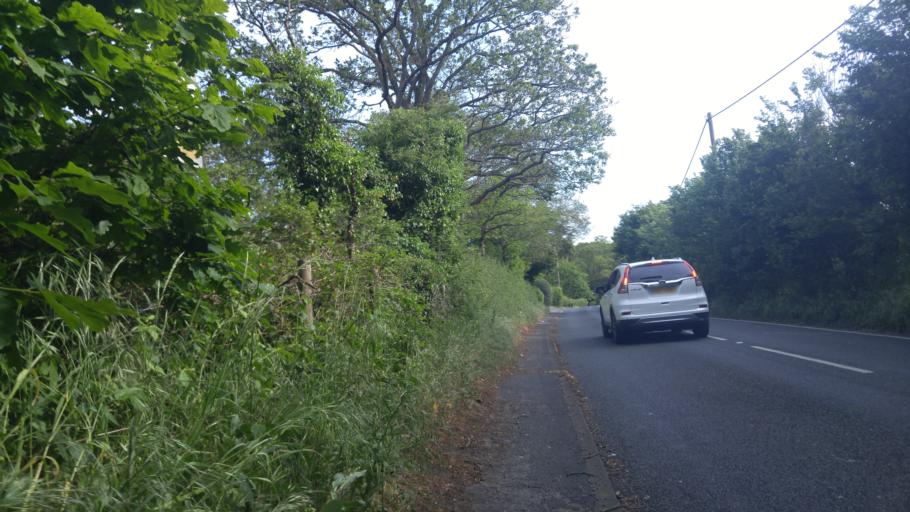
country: GB
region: England
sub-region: Essex
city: Layer de la Haye
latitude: 51.8568
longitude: 0.8646
